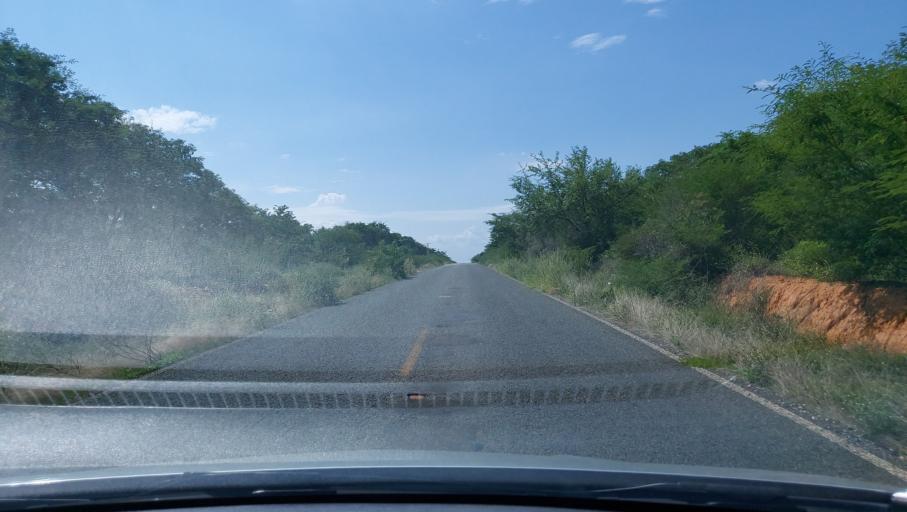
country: BR
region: Bahia
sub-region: Oliveira Dos Brejinhos
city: Beira Rio
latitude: -12.1755
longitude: -42.5440
